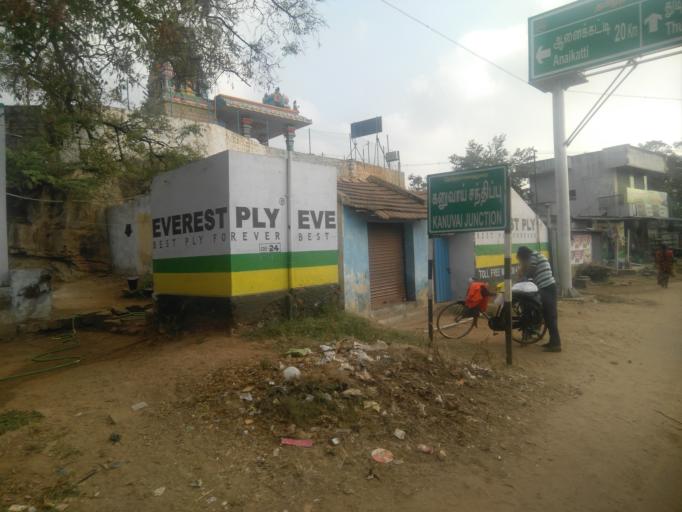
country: IN
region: Tamil Nadu
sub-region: Coimbatore
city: Coimbatore
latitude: 11.0647
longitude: 76.9076
